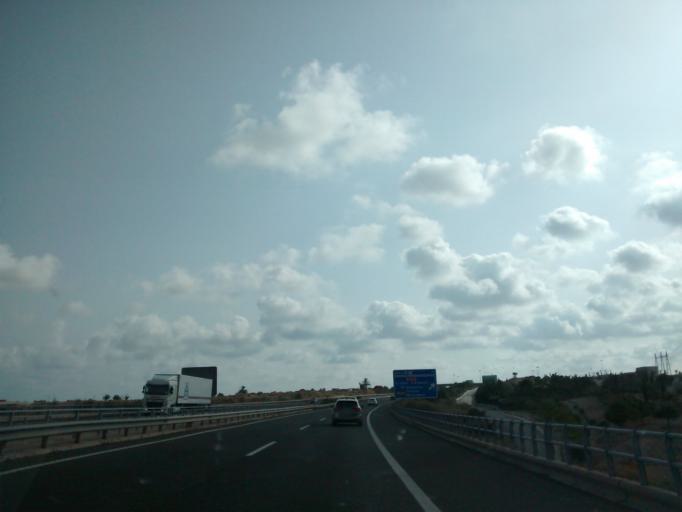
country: ES
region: Valencia
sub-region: Provincia de Alicante
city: el Campello
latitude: 38.4274
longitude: -0.4156
